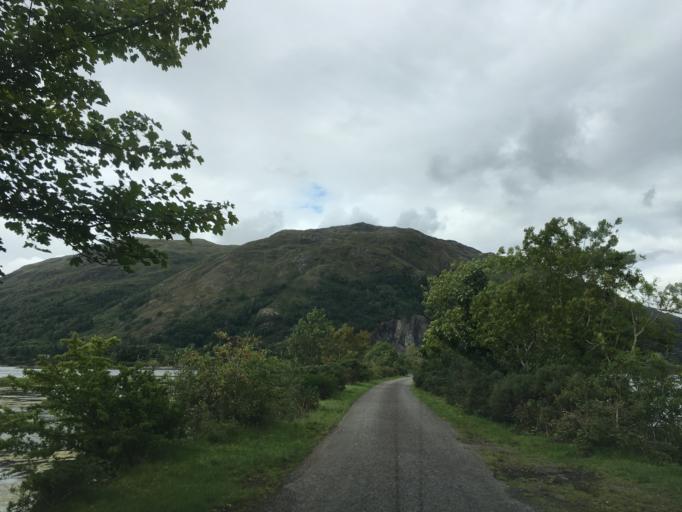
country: GB
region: Scotland
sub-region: Argyll and Bute
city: Oban
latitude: 56.4418
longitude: -5.2296
